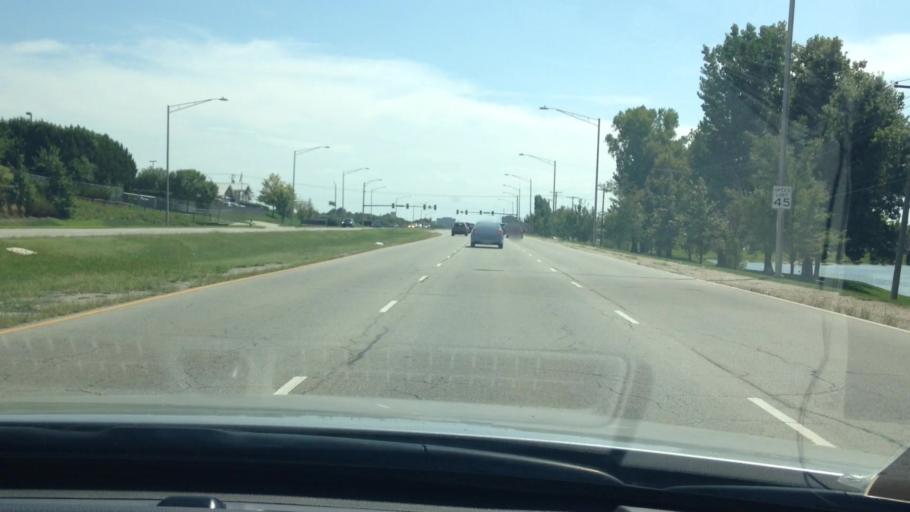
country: US
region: Kansas
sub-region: Johnson County
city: Overland Park
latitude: 38.9592
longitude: -94.6678
